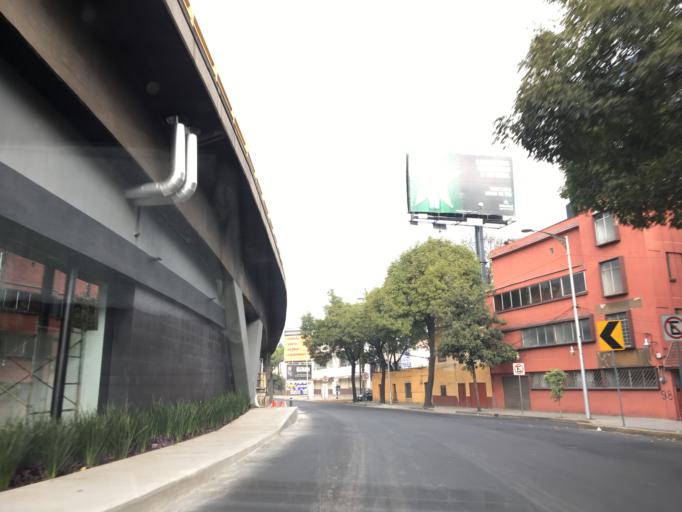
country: MX
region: Mexico City
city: Miguel Hidalgo
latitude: 19.4427
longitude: -99.1925
